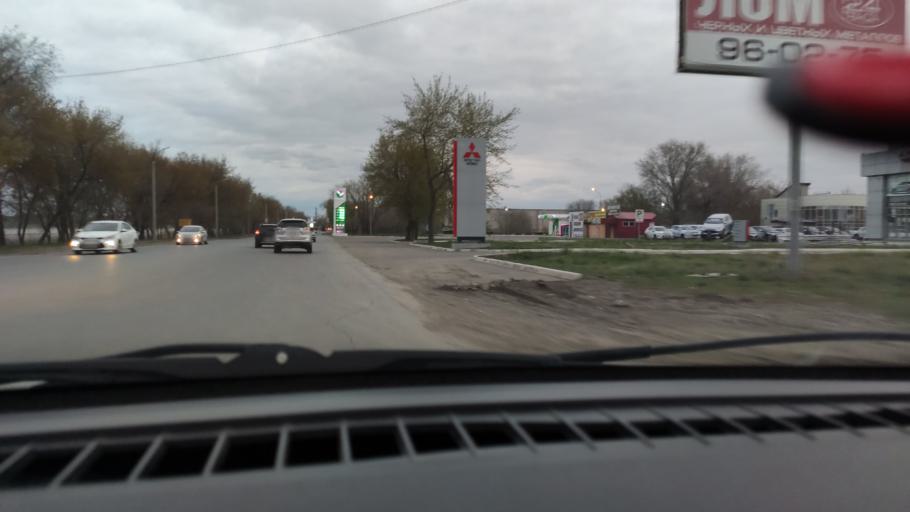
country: RU
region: Orenburg
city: Orenburg
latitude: 51.8313
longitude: 55.1092
